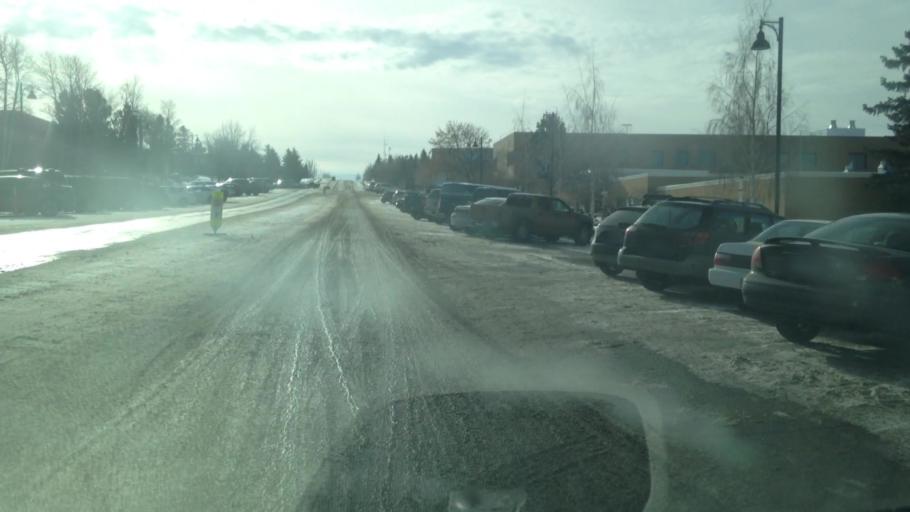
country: US
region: Idaho
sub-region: Madison County
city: Rexburg
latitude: 43.8164
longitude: -111.7838
